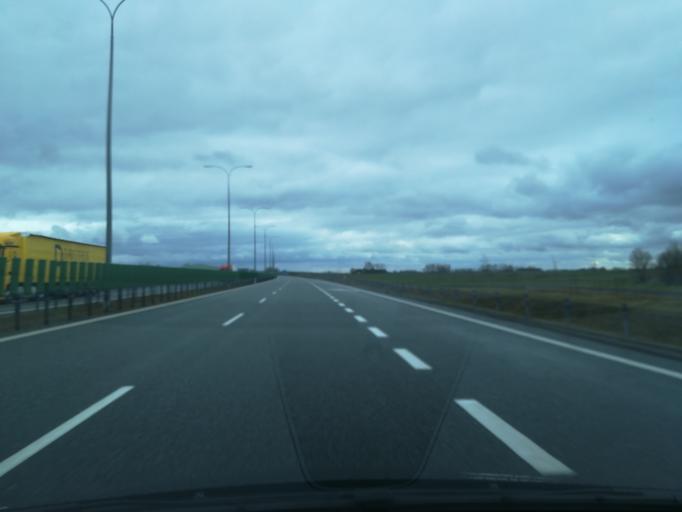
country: PL
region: Kujawsko-Pomorskie
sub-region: Powiat chelminski
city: Lisewo
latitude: 53.2854
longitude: 18.7091
